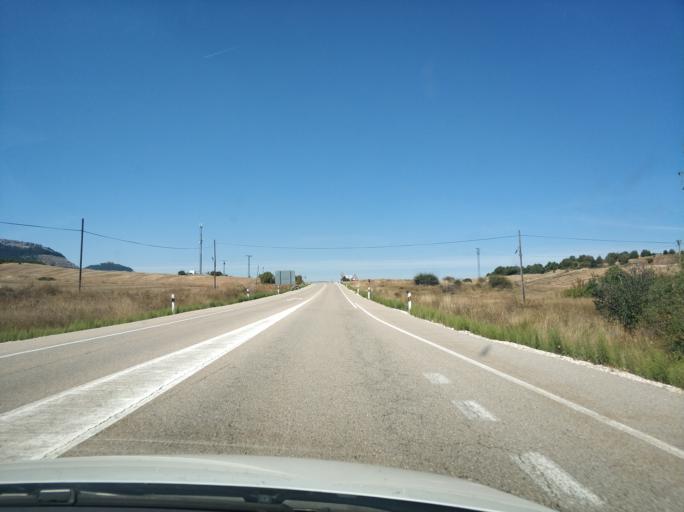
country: ES
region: Castille and Leon
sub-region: Provincia de Burgos
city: Mambrillas de Lara
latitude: 42.0922
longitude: -3.4653
